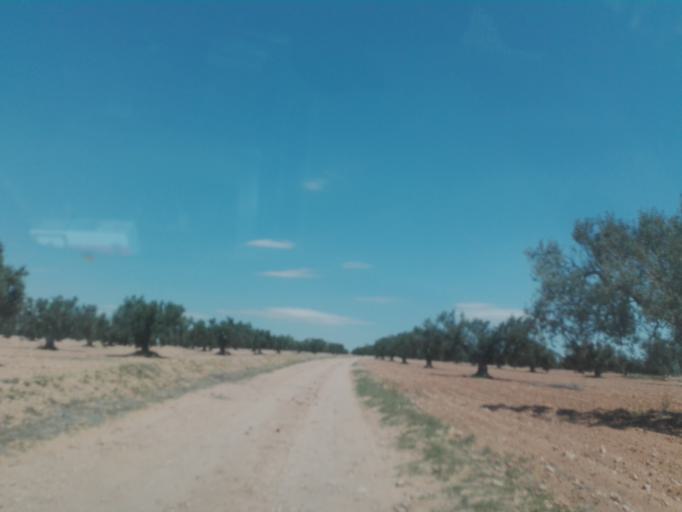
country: TN
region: Safaqis
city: Sfax
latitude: 34.6694
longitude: 10.6066
